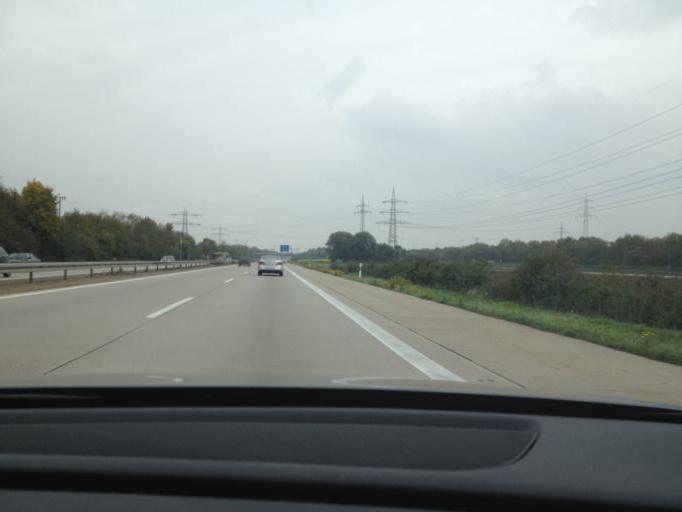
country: DE
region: Baden-Wuerttemberg
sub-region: Karlsruhe Region
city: Bruhl
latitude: 49.3892
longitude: 8.5440
